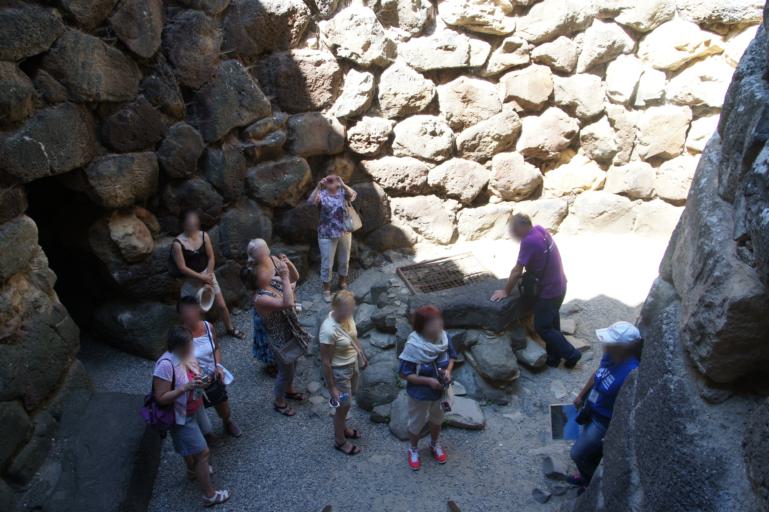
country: IT
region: Sardinia
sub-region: Provincia di Medio Campidano
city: Barumini
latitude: 39.7058
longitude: 8.9908
